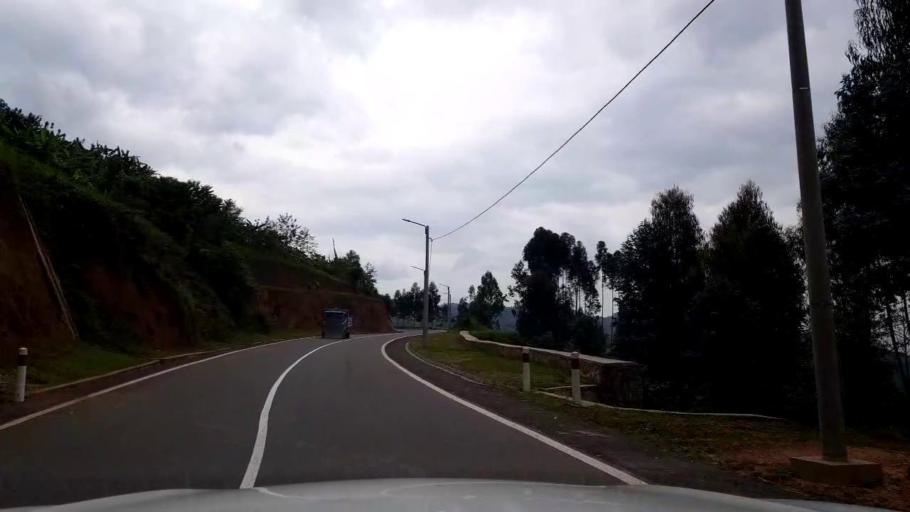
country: RW
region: Western Province
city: Kibuye
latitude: -1.9299
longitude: 29.3723
